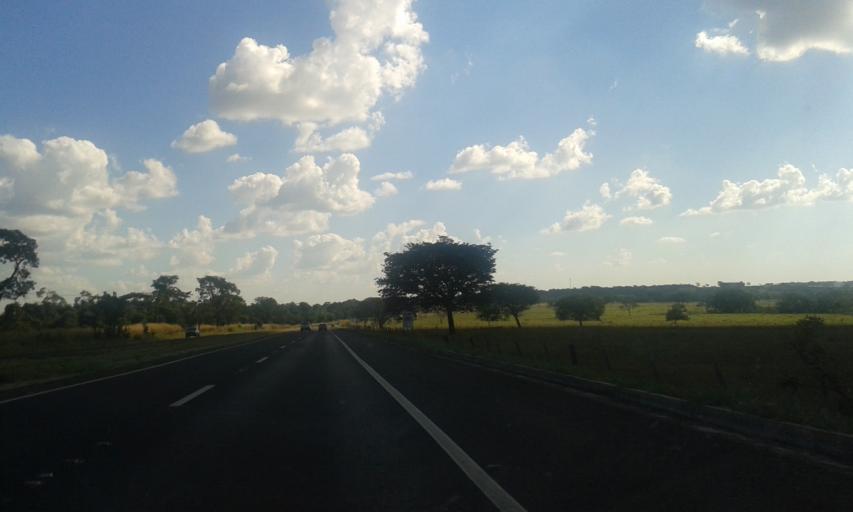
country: BR
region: Minas Gerais
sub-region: Monte Alegre De Minas
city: Monte Alegre de Minas
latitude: -18.8937
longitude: -48.6501
